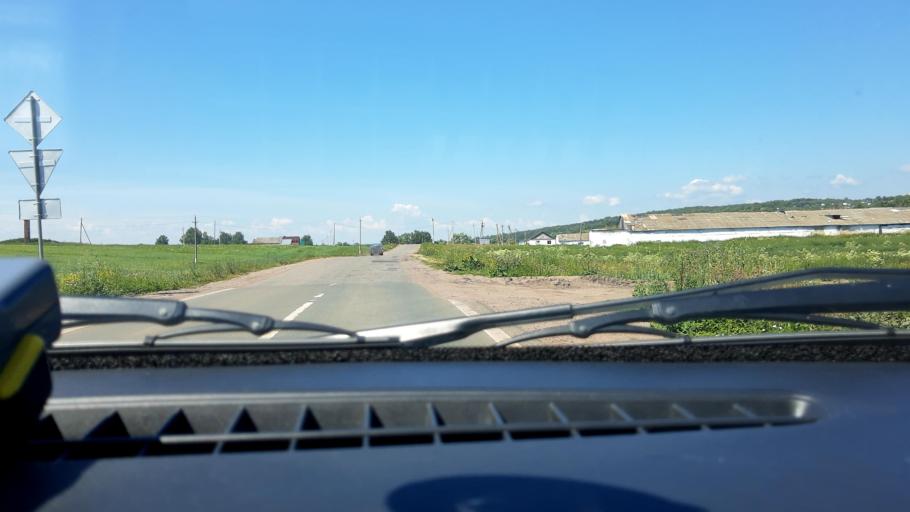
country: RU
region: Bashkortostan
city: Karmaskaly
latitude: 54.3572
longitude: 55.9114
